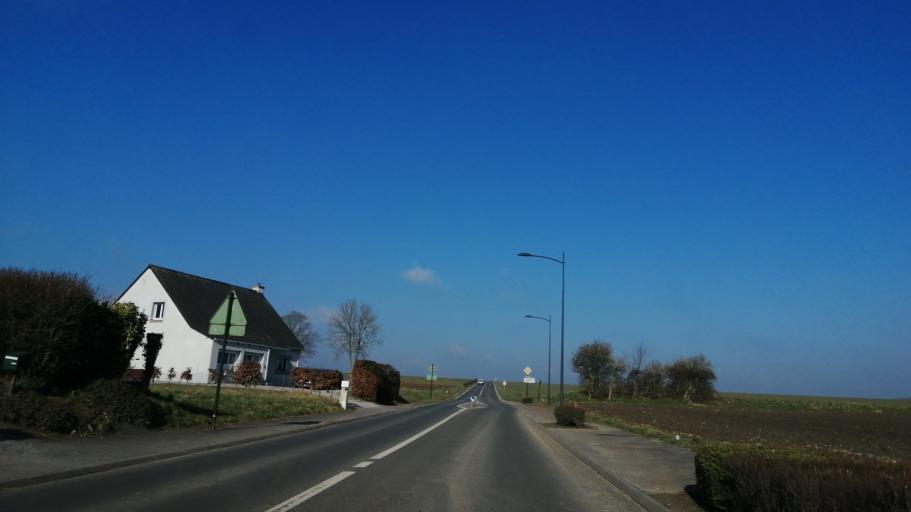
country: FR
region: Nord-Pas-de-Calais
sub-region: Departement du Pas-de-Calais
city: Ranchicourt
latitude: 50.4167
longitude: 2.5786
